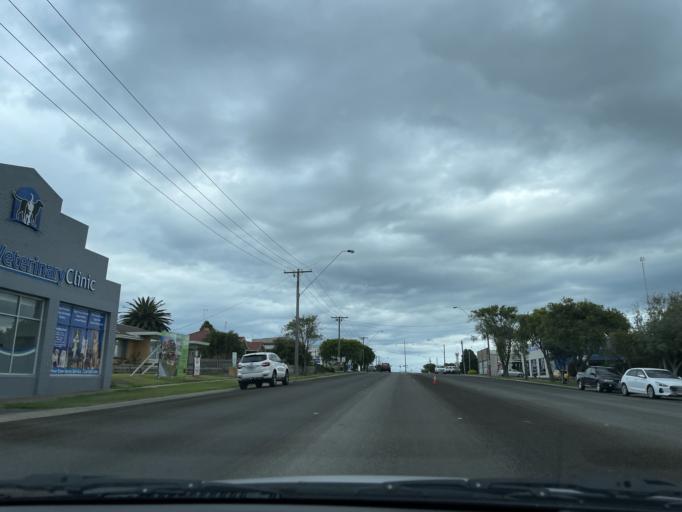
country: AU
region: Victoria
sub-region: Glenelg
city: Portland
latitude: -38.3383
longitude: 141.6042
